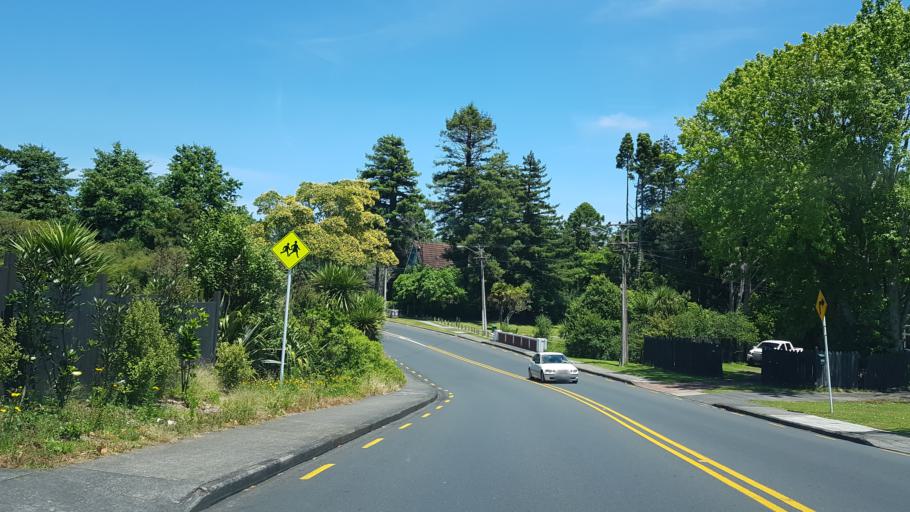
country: NZ
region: Auckland
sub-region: Auckland
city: Waitakere
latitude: -36.9114
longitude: 174.6490
